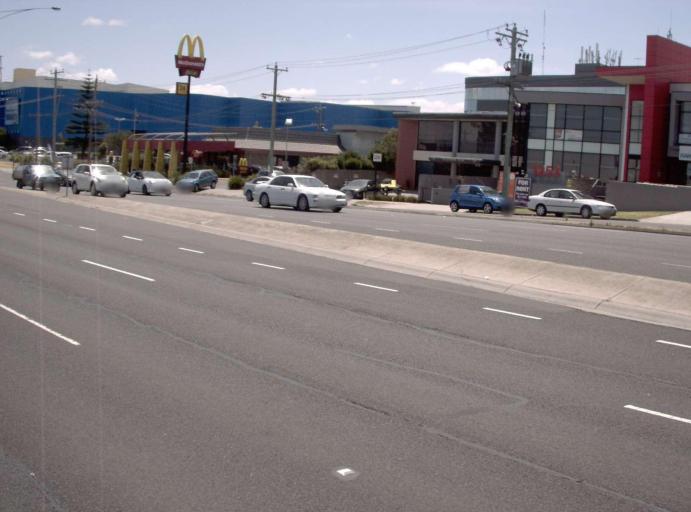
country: AU
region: Victoria
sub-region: Bayside
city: Cheltenham
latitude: -37.9615
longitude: 145.0547
